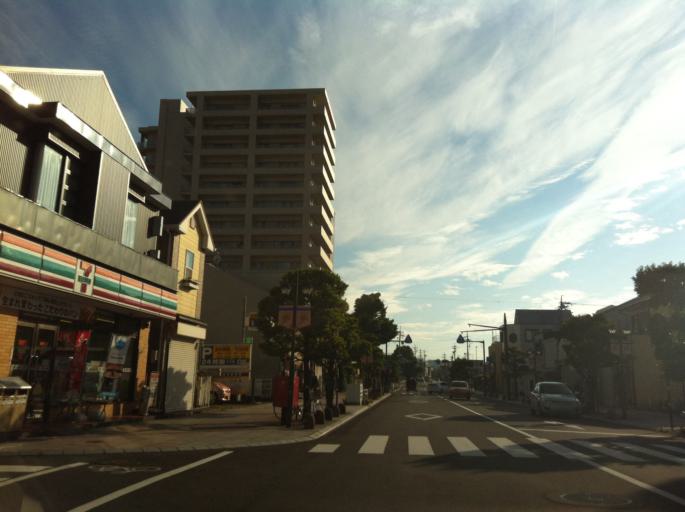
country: JP
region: Shizuoka
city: Shizuoka-shi
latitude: 35.0051
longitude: 138.4948
